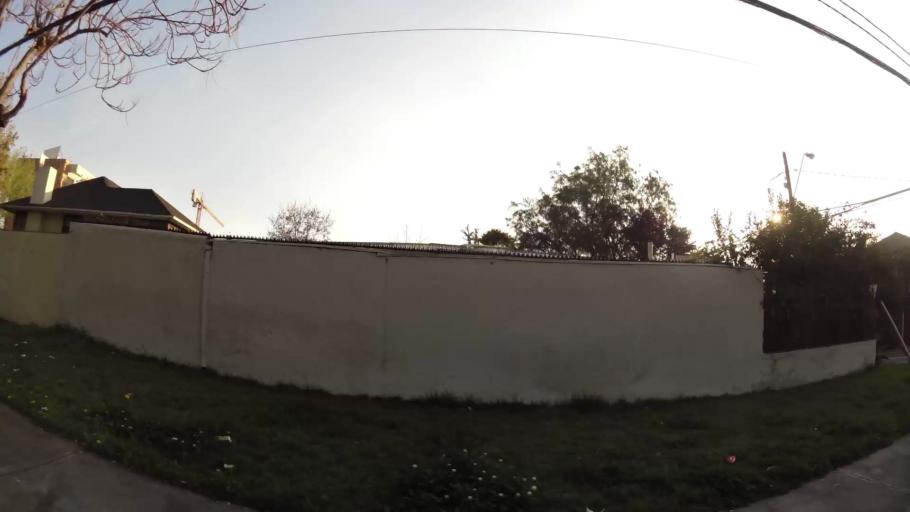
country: CL
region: Santiago Metropolitan
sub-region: Provincia de Santiago
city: Villa Presidente Frei, Nunoa, Santiago, Chile
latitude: -33.3941
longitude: -70.5494
